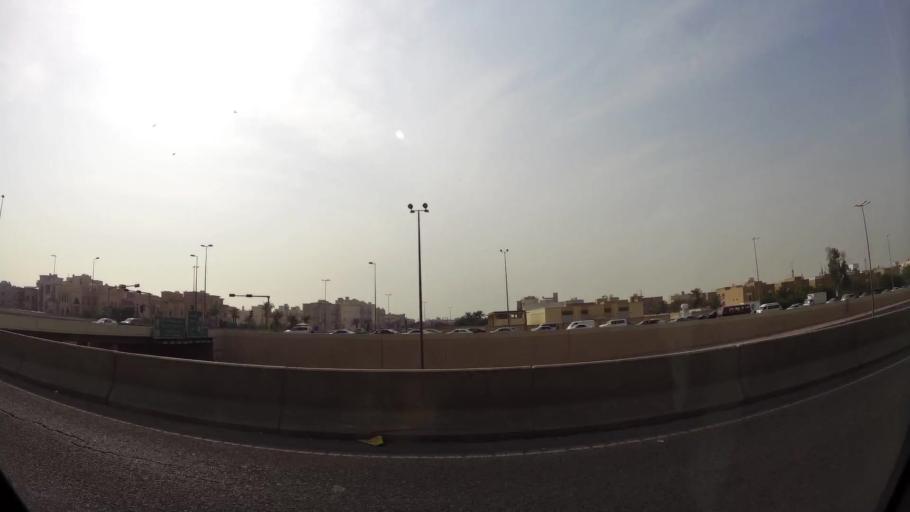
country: KW
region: Al Farwaniyah
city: Al Farwaniyah
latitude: 29.2803
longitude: 47.9498
